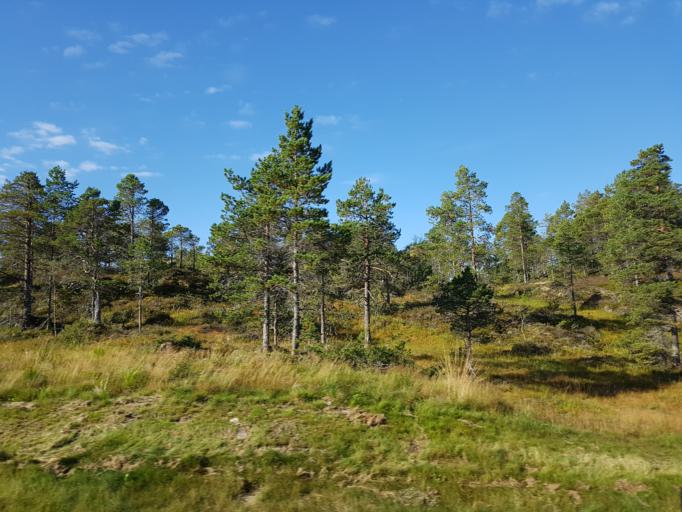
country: NO
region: Sor-Trondelag
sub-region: Trondheim
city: Trondheim
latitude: 63.6407
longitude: 10.2703
